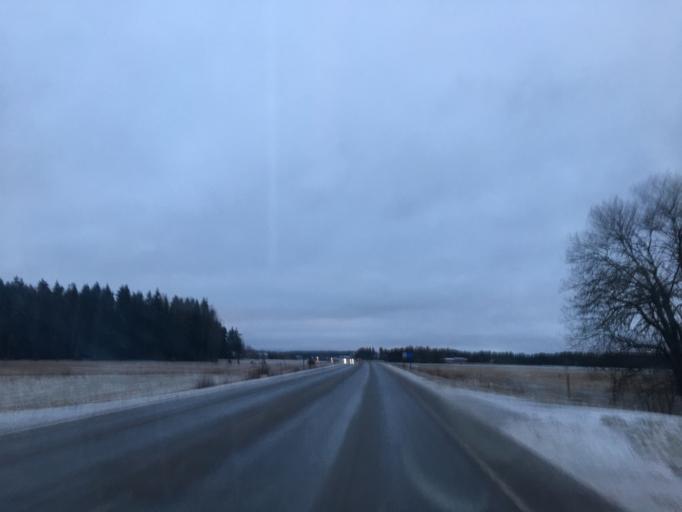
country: FI
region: Varsinais-Suomi
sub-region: Loimaa
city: Aura
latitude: 60.6606
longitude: 22.5594
